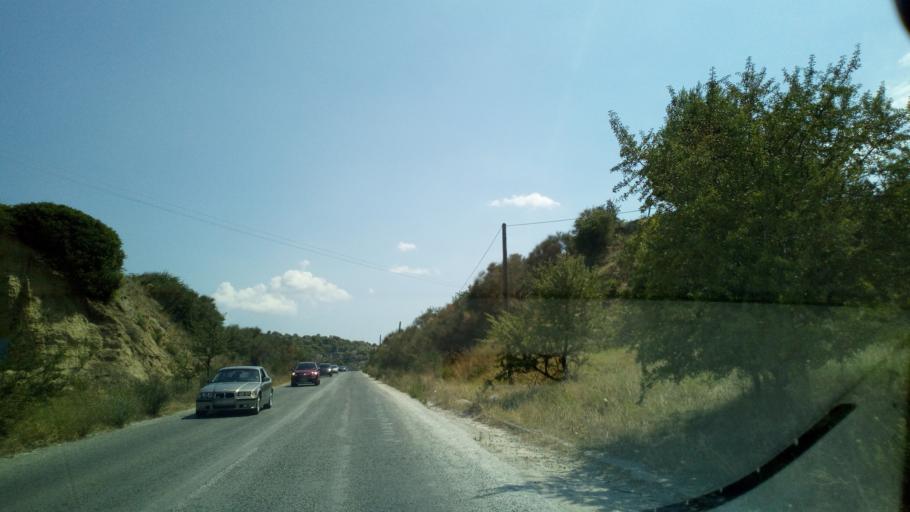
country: GR
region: Central Macedonia
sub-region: Nomos Chalkidikis
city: Agios Nikolaos
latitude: 40.2260
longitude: 23.7002
